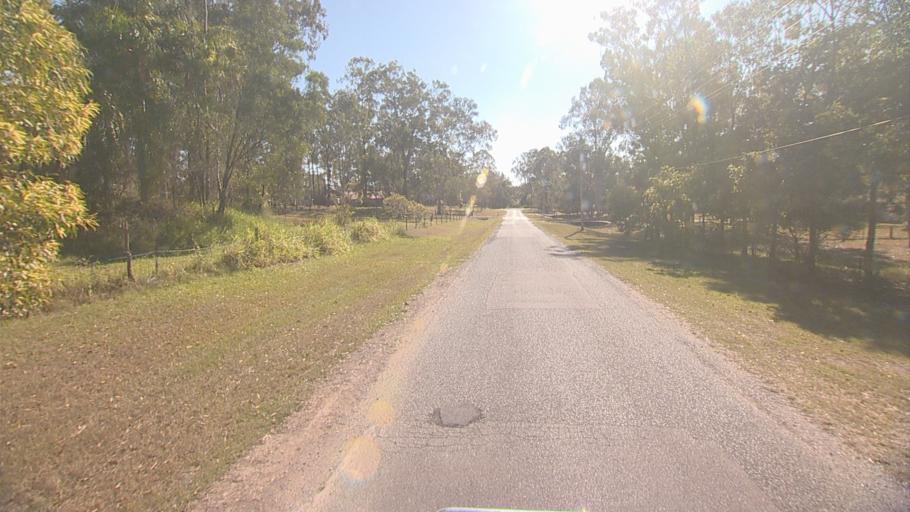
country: AU
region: Queensland
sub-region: Logan
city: Cedar Vale
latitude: -27.8263
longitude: 153.0481
